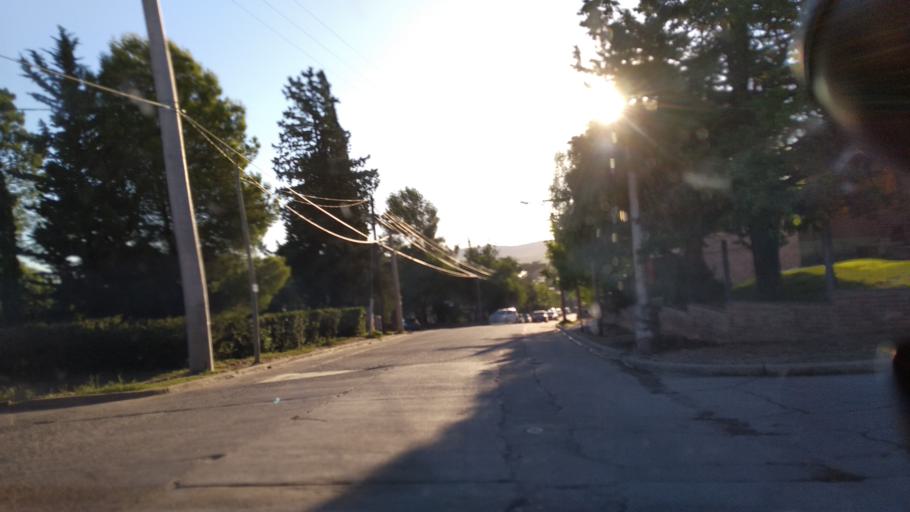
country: AR
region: Cordoba
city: Mina Clavero
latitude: -31.7204
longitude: -65.0021
